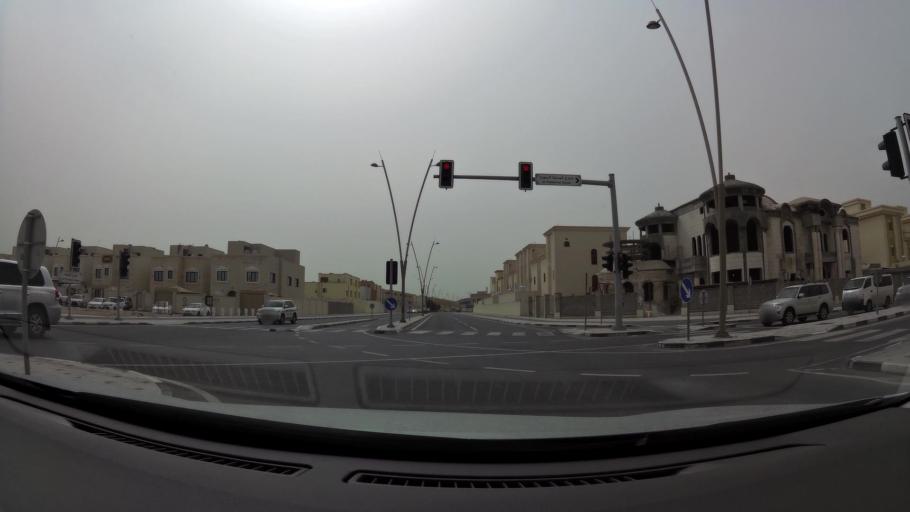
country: QA
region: Baladiyat ad Dawhah
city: Doha
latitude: 25.2310
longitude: 51.5421
